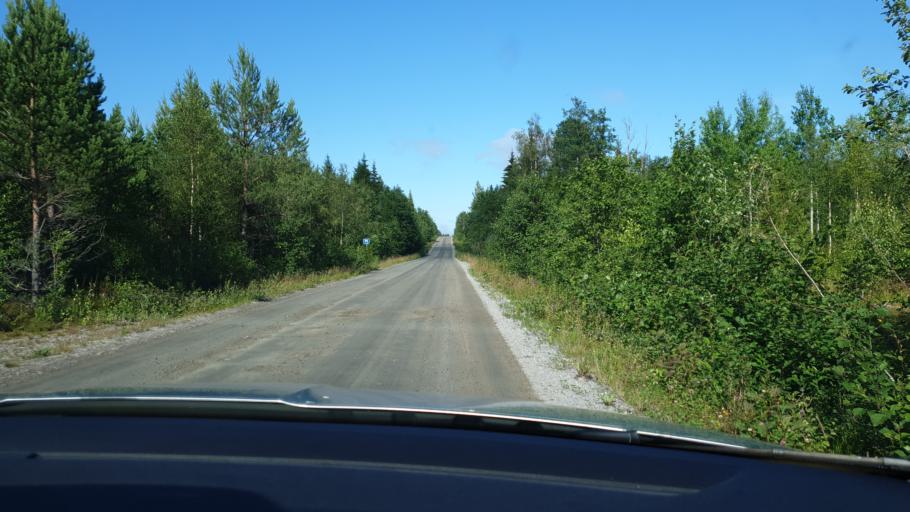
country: SE
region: Gaevleborg
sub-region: Soderhamns Kommun
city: Soderhamn
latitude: 61.4286
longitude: 16.9945
